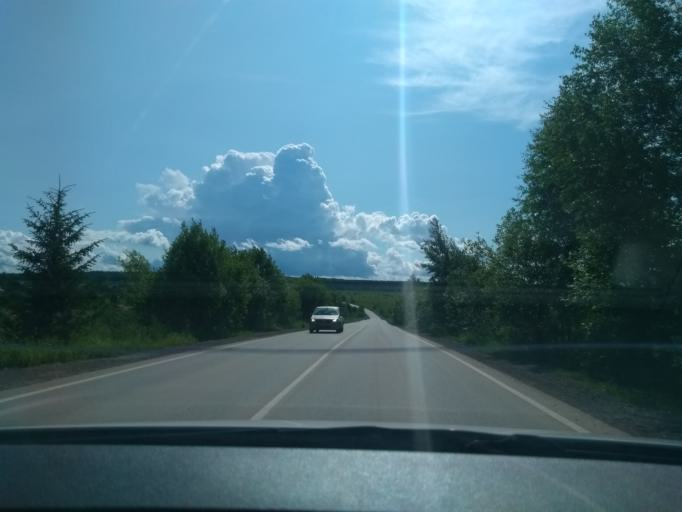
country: RU
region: Perm
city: Bershet'
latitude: 57.8134
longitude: 56.4524
